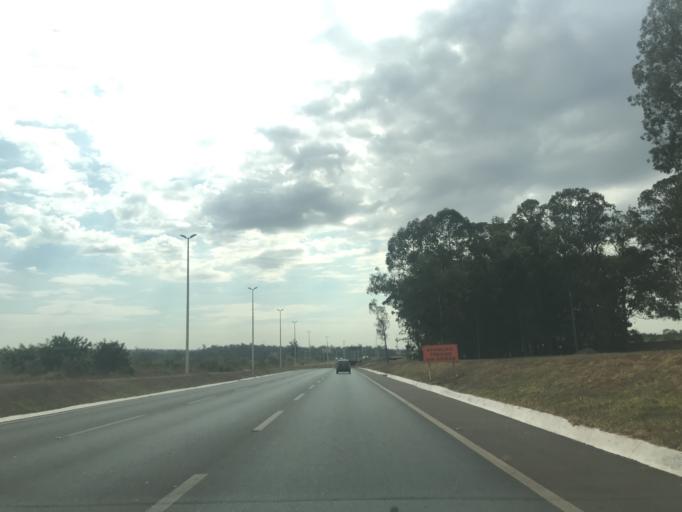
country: BR
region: Federal District
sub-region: Brasilia
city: Brasilia
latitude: -15.8606
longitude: -47.9368
